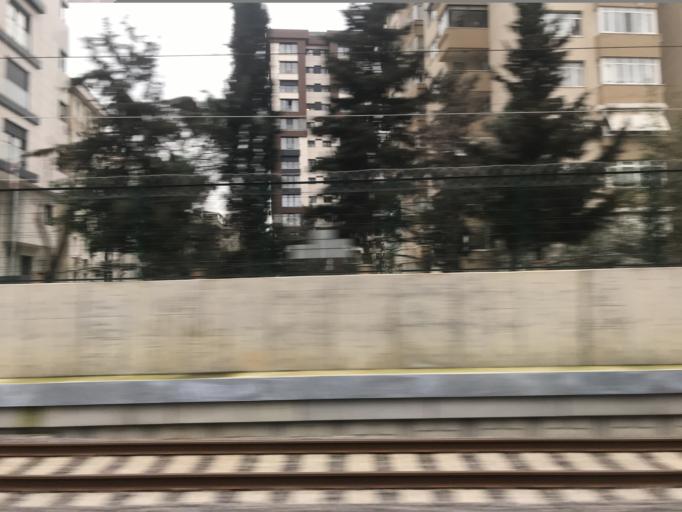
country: TR
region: Istanbul
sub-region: Atasehir
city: Atasehir
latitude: 40.9777
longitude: 29.0689
